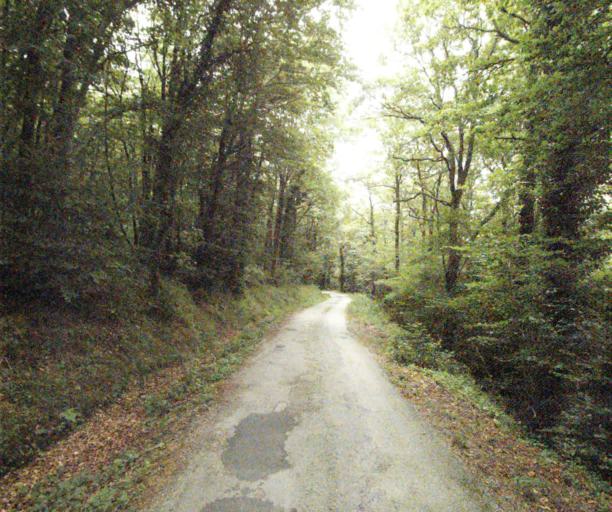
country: FR
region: Midi-Pyrenees
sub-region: Departement du Tarn
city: Soreze
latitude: 43.4313
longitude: 2.0900
